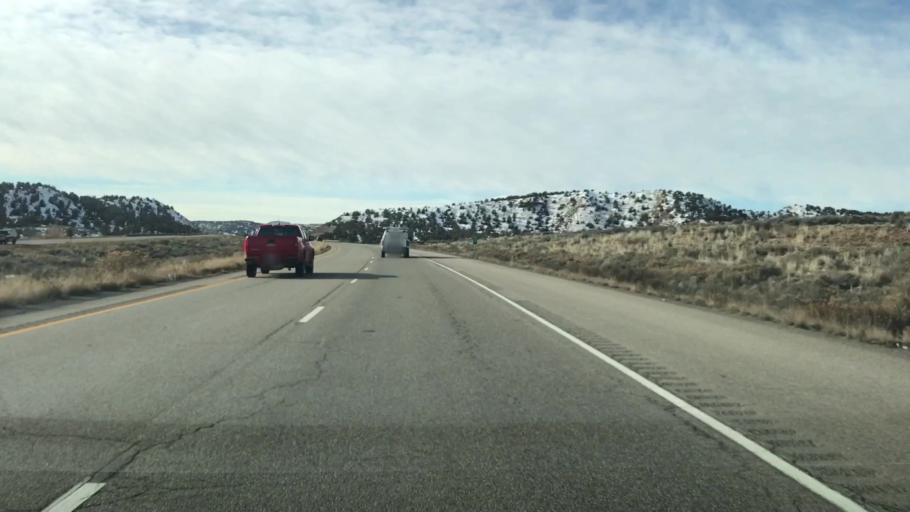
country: US
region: Colorado
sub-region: Garfield County
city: Parachute
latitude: 39.3839
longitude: -108.1511
